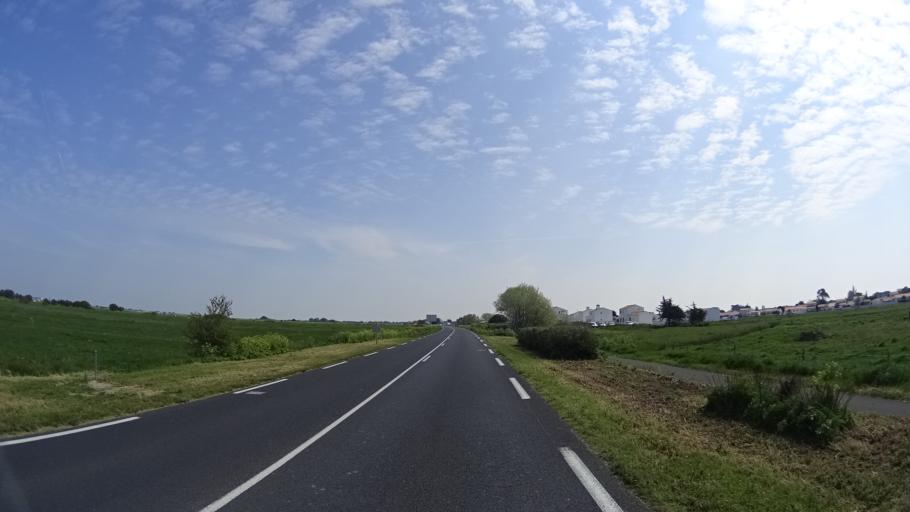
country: FR
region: Pays de la Loire
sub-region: Departement de la Vendee
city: La Gueriniere
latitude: 46.9851
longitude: -2.2750
